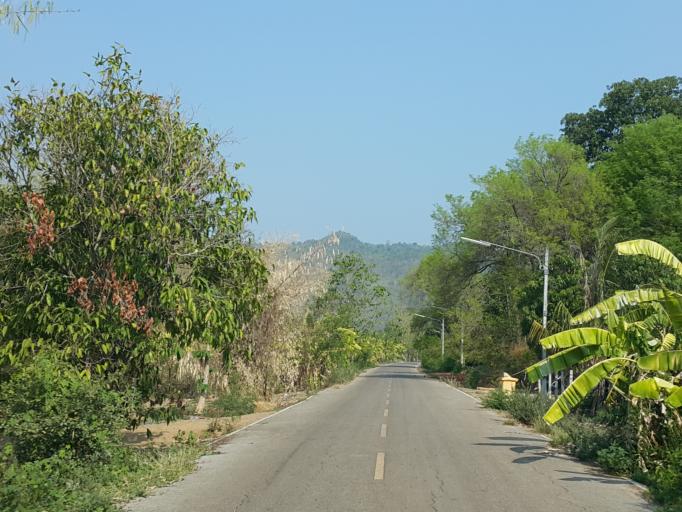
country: TH
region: Kanchanaburi
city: Sai Yok
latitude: 14.1232
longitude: 99.1348
